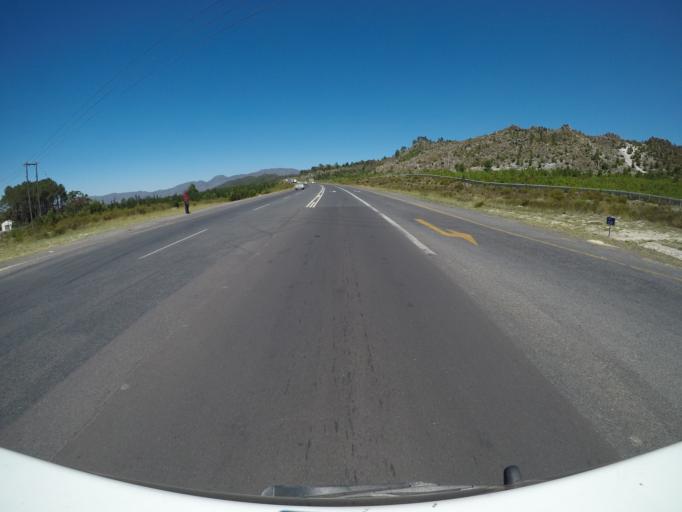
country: ZA
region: Western Cape
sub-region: Overberg District Municipality
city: Grabouw
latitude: -34.1631
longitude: 19.0081
